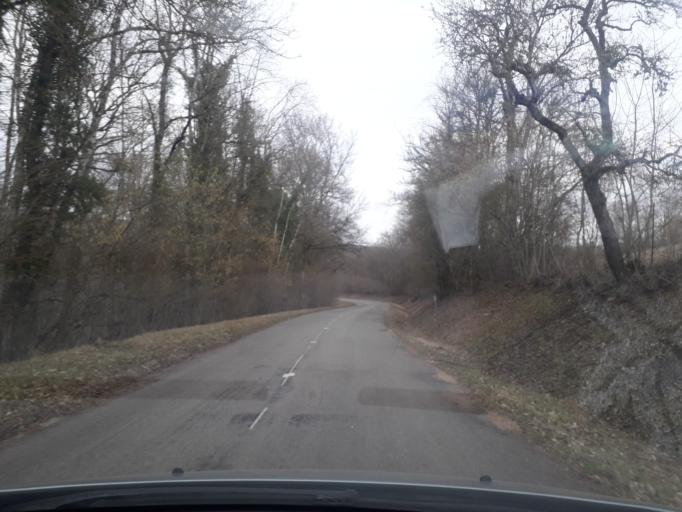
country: FR
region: Bourgogne
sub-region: Departement de la Cote-d'Or
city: Messigny-et-Vantoux
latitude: 47.4747
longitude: 4.9564
